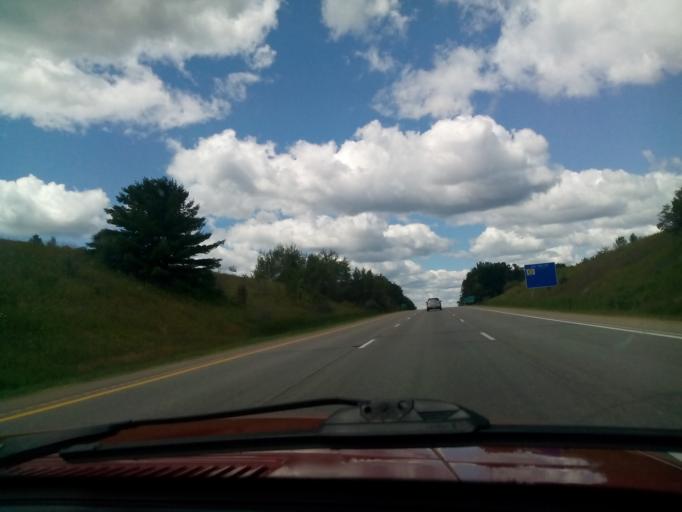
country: US
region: Michigan
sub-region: Ogemaw County
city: West Branch
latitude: 44.2668
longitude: -84.2704
